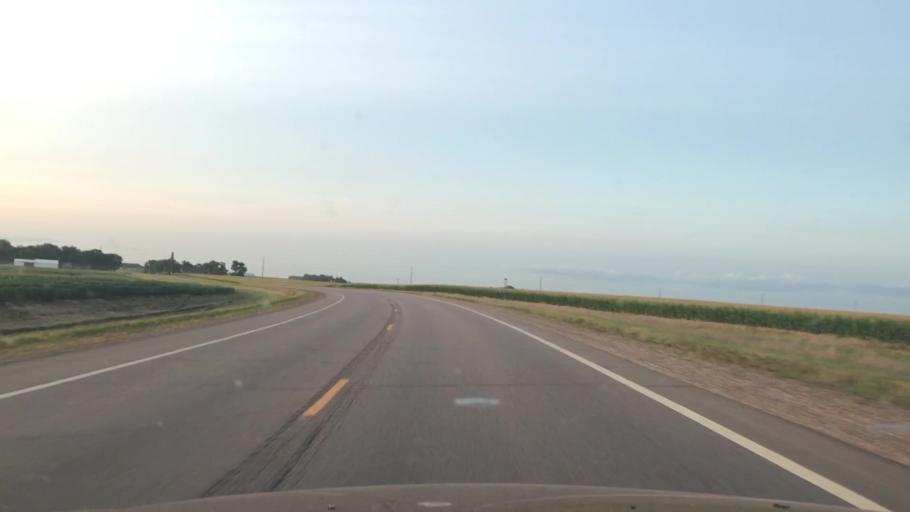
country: US
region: Minnesota
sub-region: Redwood County
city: Redwood Falls
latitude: 44.4203
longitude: -95.1180
